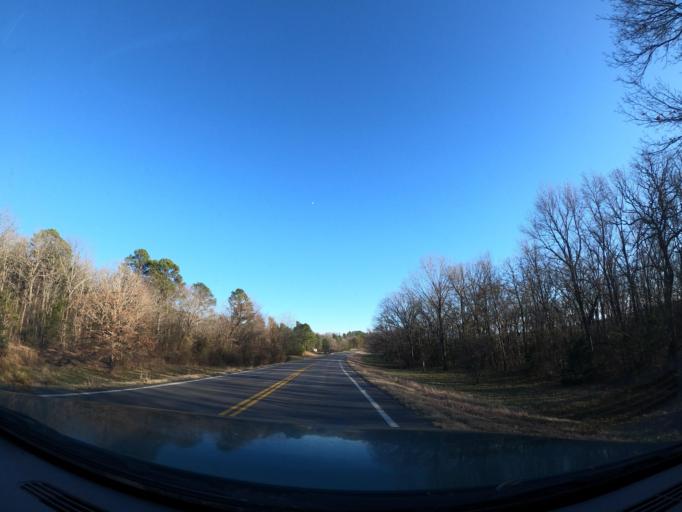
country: US
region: Oklahoma
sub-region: Latimer County
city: Wilburton
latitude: 34.9579
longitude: -95.3479
